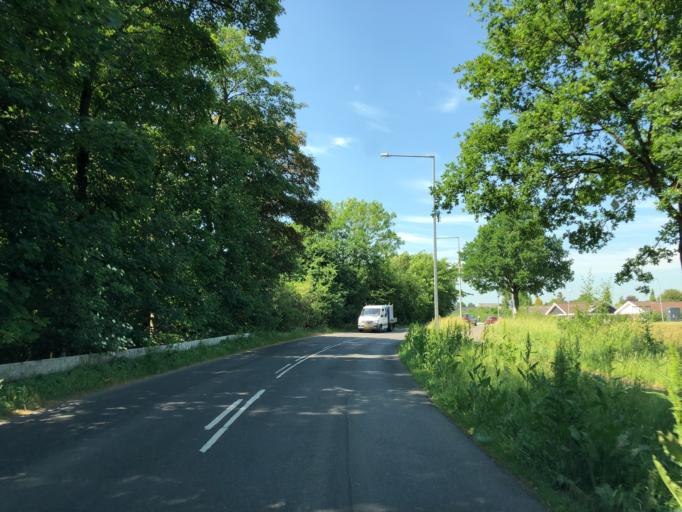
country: DK
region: South Denmark
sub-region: Kolding Kommune
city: Kolding
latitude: 55.5162
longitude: 9.4854
